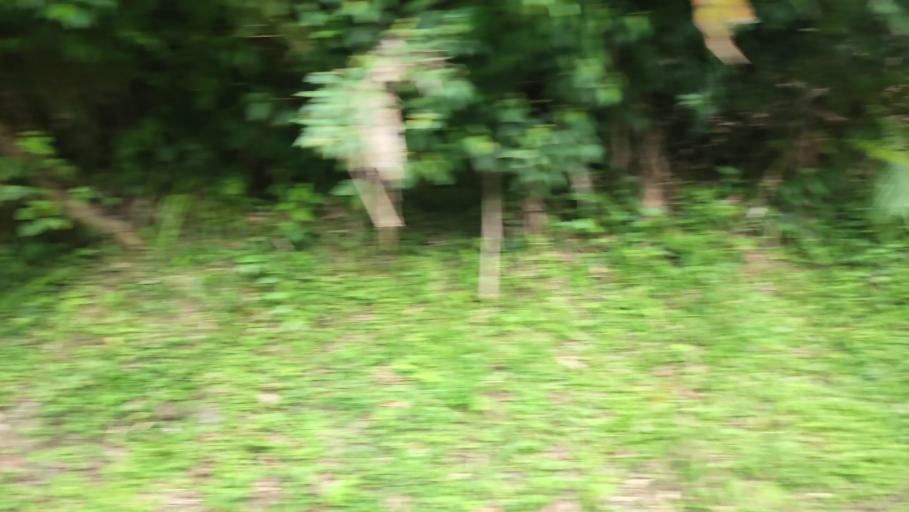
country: TW
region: Taiwan
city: Daxi
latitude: 24.8829
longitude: 121.4181
